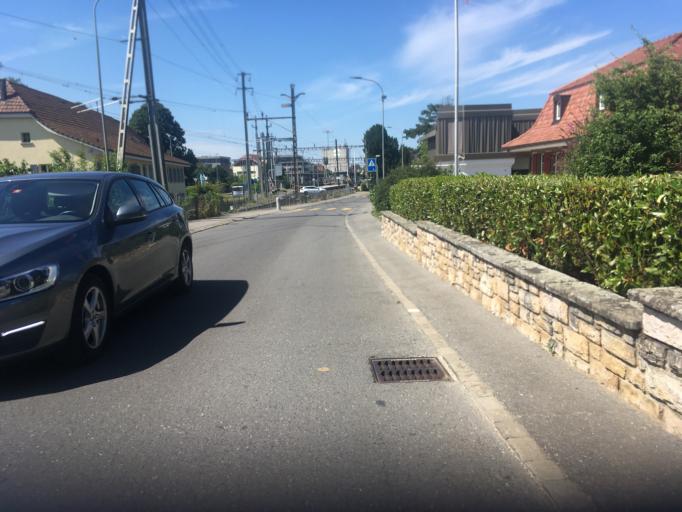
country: CH
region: Fribourg
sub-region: See District
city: Murten
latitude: 46.9264
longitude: 7.1177
